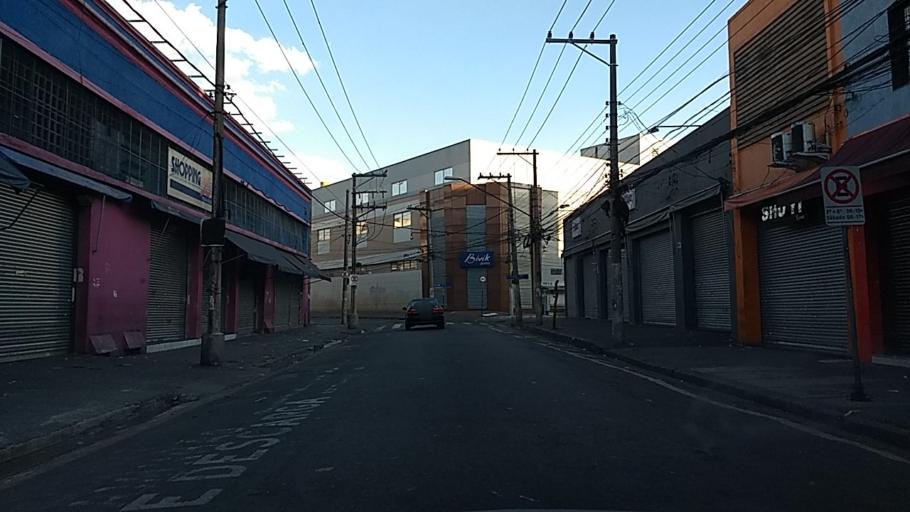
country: BR
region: Sao Paulo
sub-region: Sao Paulo
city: Sao Paulo
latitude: -23.5390
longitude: -46.6191
